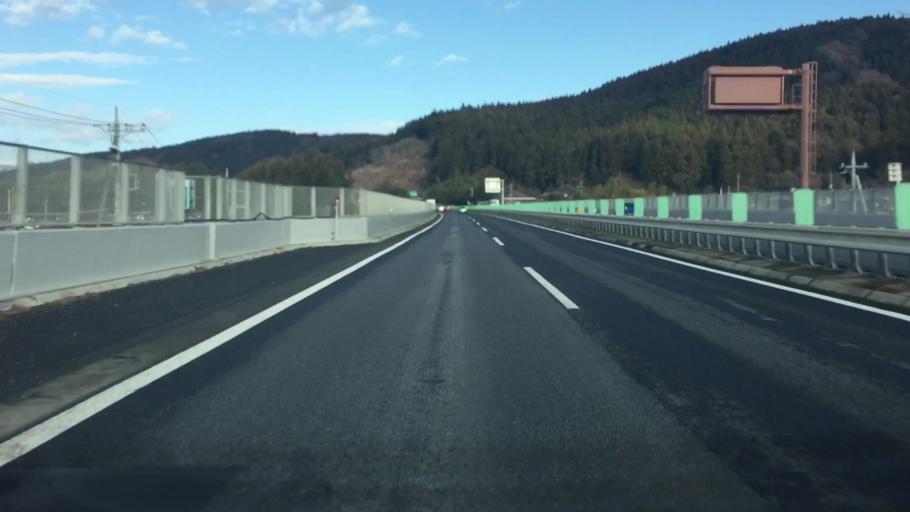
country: JP
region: Gunma
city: Annaka
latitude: 36.3194
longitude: 138.7721
